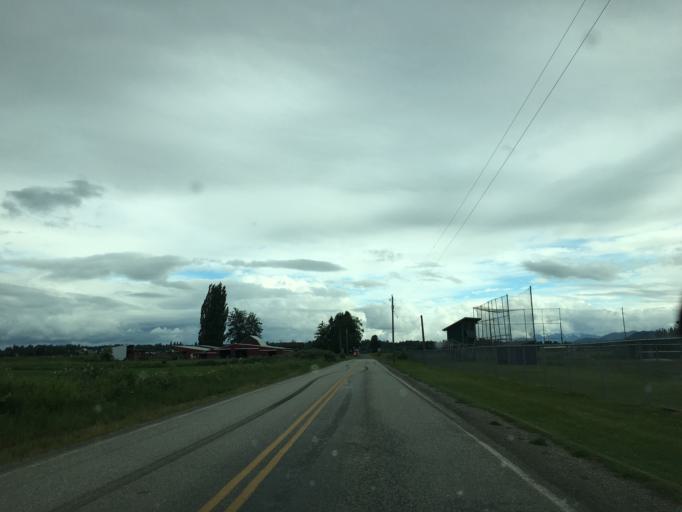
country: US
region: Washington
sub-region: Whatcom County
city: Nooksack
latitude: 48.9665
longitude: -122.3091
